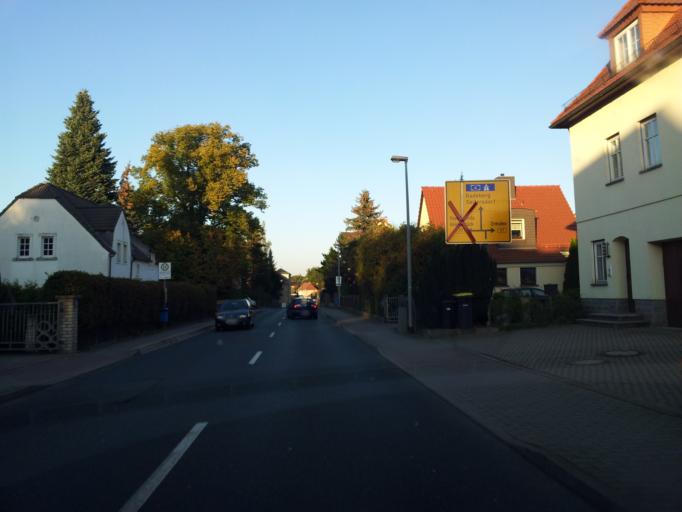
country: DE
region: Saxony
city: Ottendorf-Okrilla
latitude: 51.1862
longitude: 13.8294
